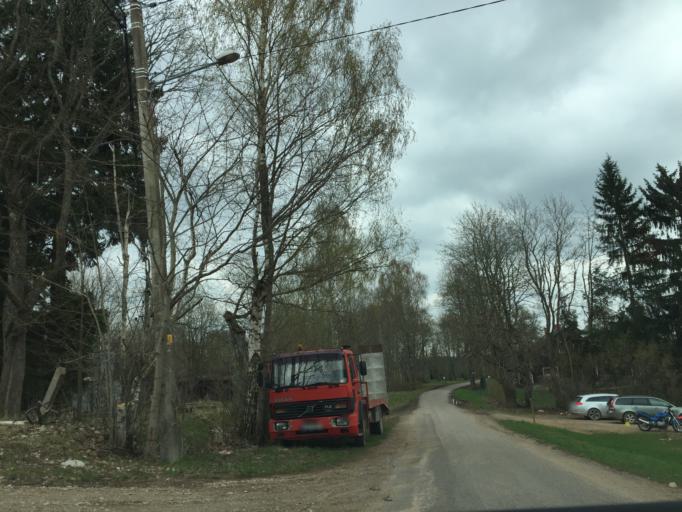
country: EE
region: Tartu
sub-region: Noo vald
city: Noo
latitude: 58.2699
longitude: 26.5385
